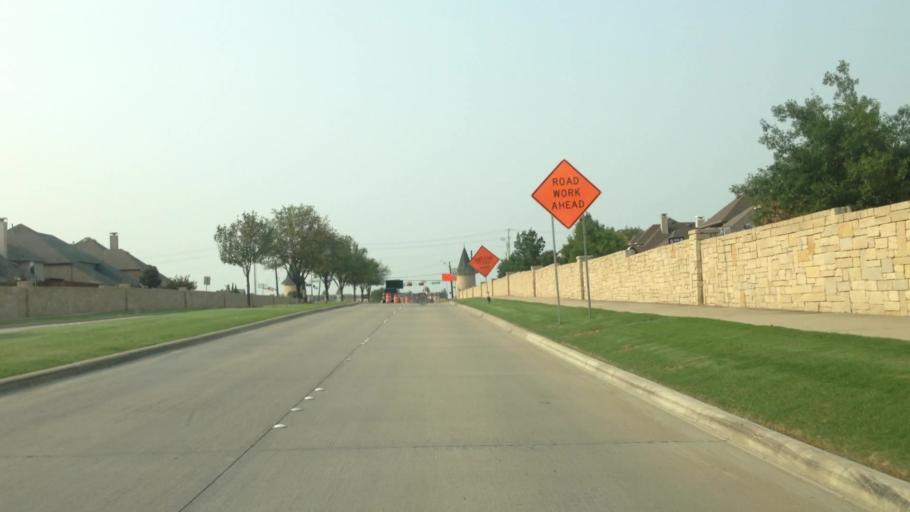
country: US
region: Texas
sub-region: Denton County
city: The Colony
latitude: 33.0443
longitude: -96.9126
